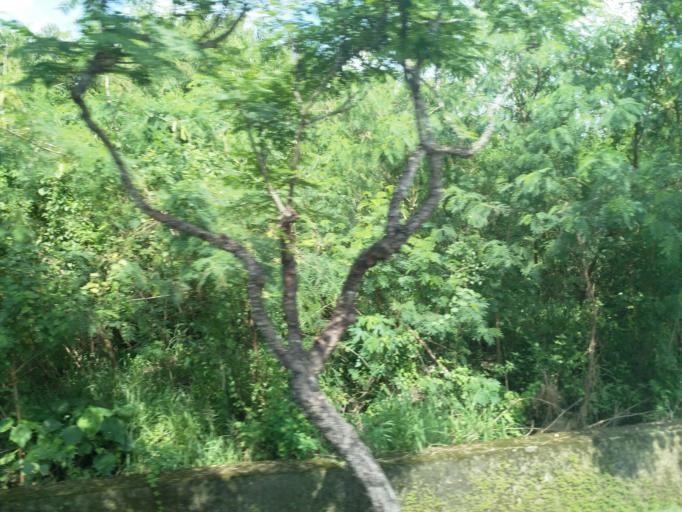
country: TW
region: Taiwan
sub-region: Pingtung
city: Pingtung
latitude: 22.8799
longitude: 120.5678
